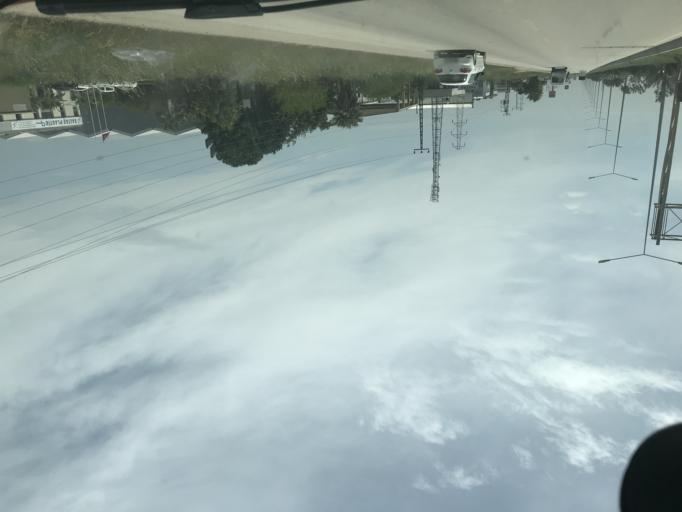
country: TR
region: Adana
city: Yuregir
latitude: 36.9824
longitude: 35.4261
